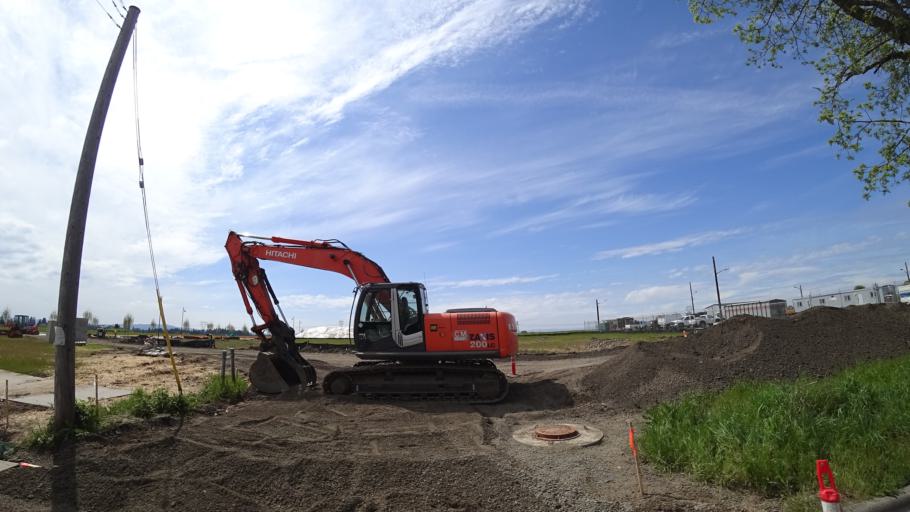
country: US
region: Oregon
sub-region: Washington County
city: Aloha
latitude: 45.4929
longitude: -122.8919
